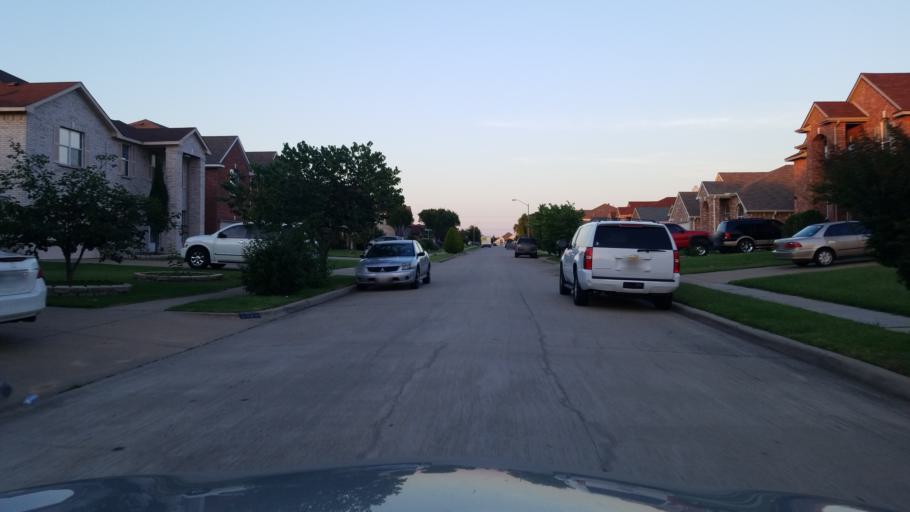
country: US
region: Texas
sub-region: Dallas County
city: Grand Prairie
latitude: 32.6908
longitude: -97.0412
